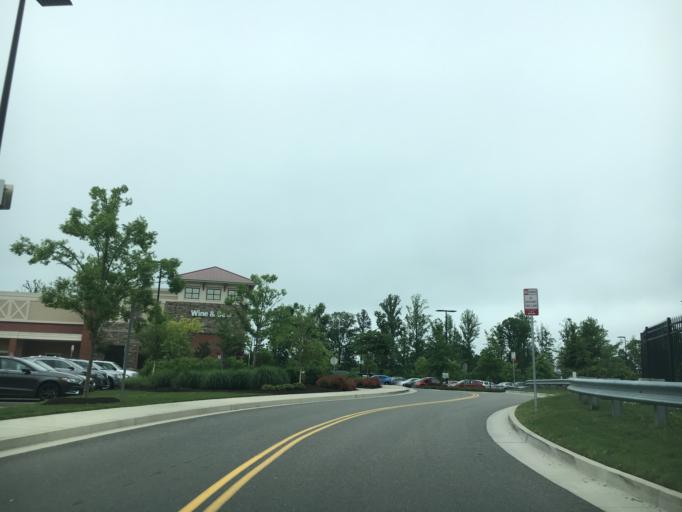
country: US
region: Virginia
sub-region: Henrico County
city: Short Pump
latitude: 37.6621
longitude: -77.6350
